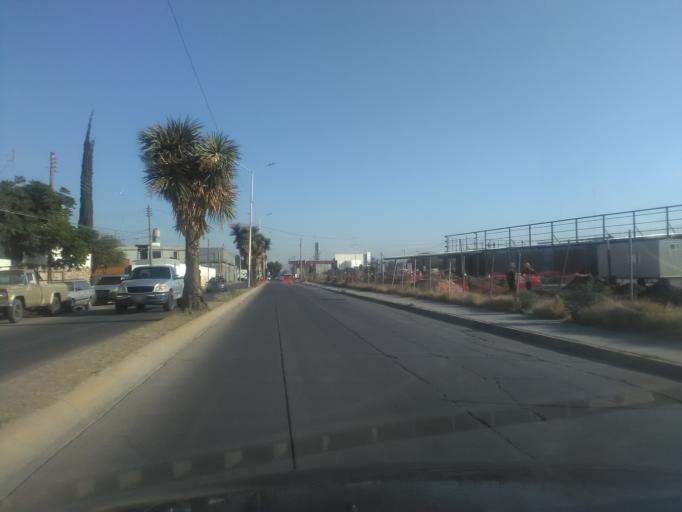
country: MX
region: Durango
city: Victoria de Durango
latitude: 24.0451
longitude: -104.6229
